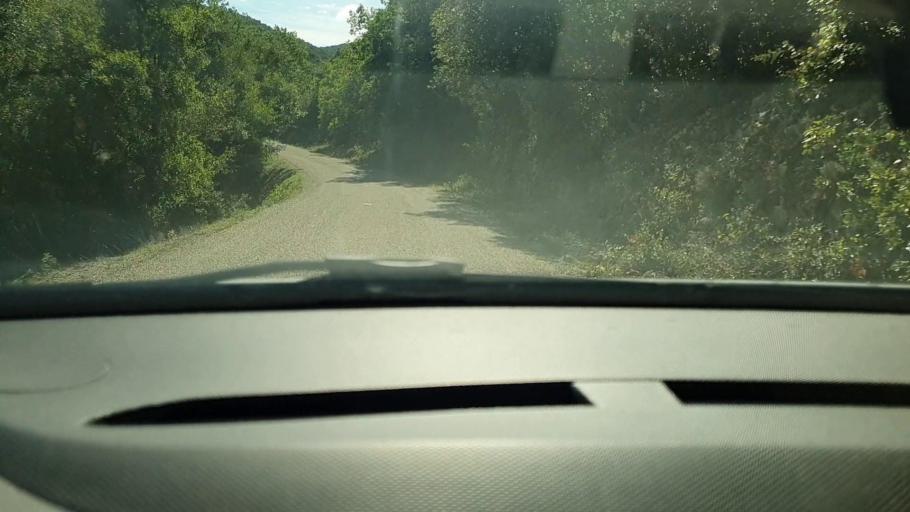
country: FR
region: Languedoc-Roussillon
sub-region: Departement du Gard
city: Barjac
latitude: 44.2138
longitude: 4.2973
